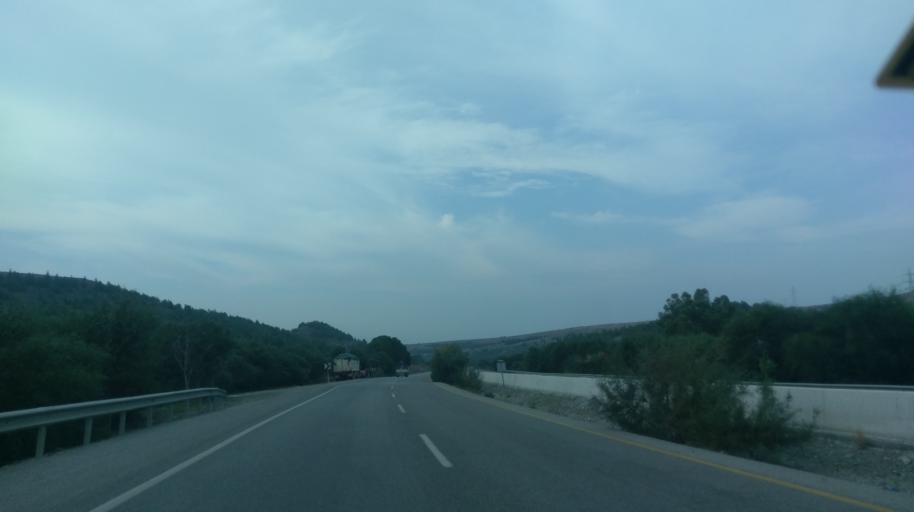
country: CY
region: Lefkosia
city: Akaki
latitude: 35.2099
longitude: 33.1243
